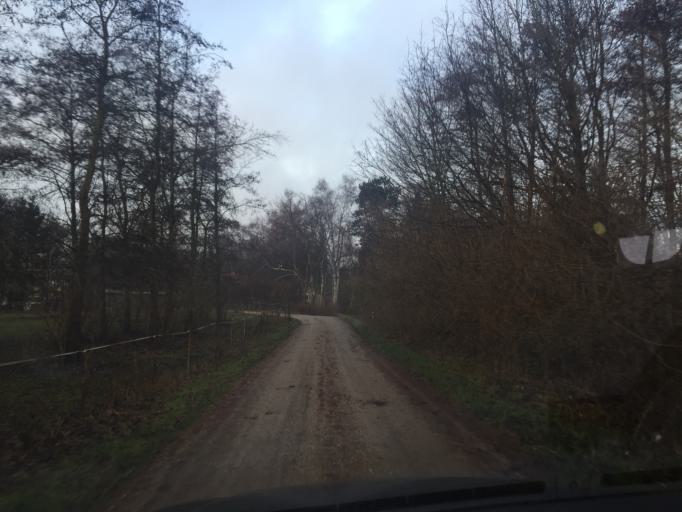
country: DK
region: Capital Region
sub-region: Hoje-Taastrup Kommune
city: Flong
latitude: 55.6857
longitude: 12.2321
